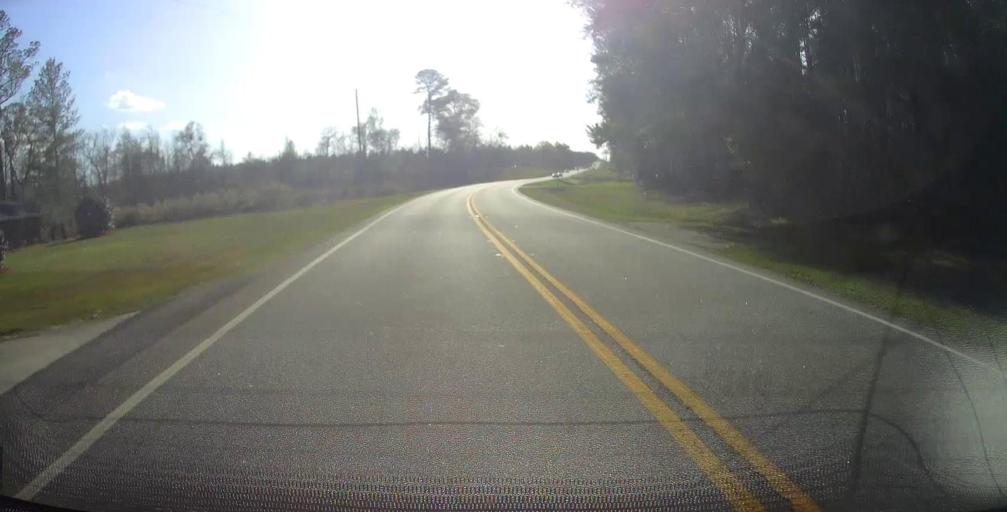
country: US
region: Georgia
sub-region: Montgomery County
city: Mount Vernon
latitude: 32.1742
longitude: -82.6786
